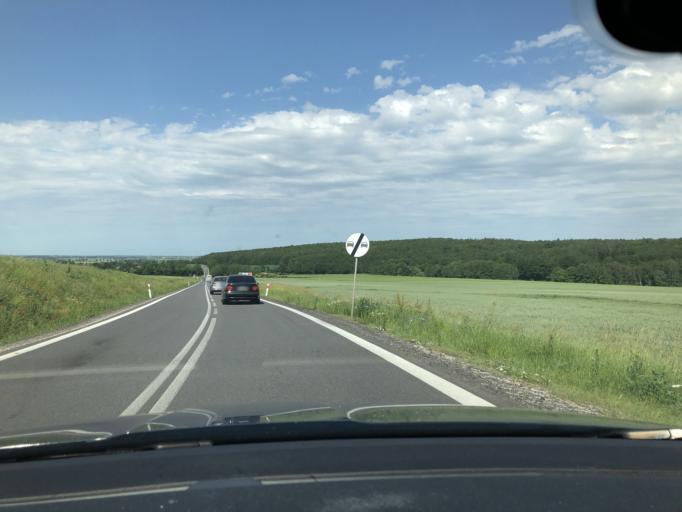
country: PL
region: Lower Silesian Voivodeship
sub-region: Powiat jaworski
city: Bolkow
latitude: 50.9556
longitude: 16.1418
